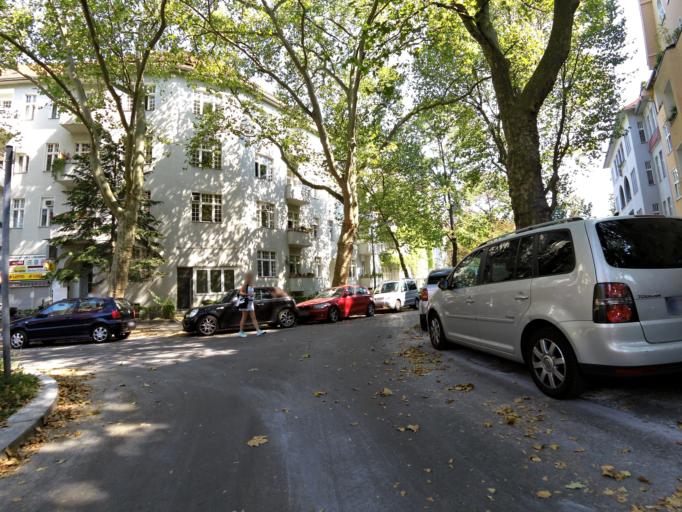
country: DE
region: Berlin
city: Friedenau
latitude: 52.4701
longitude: 13.3203
